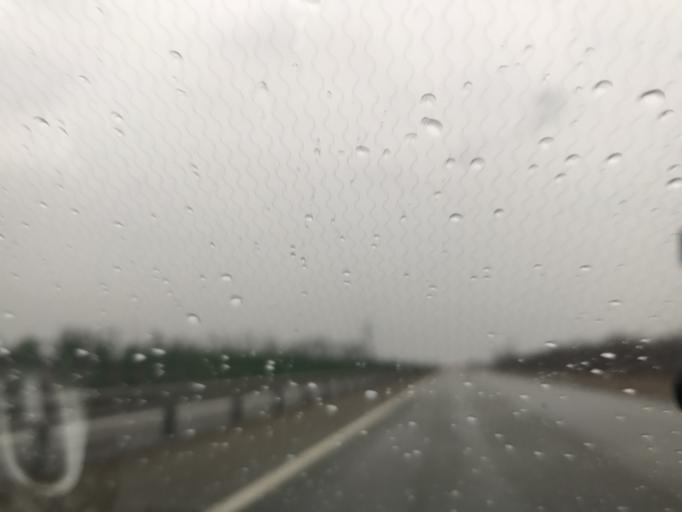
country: RU
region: Krasnodarskiy
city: Krylovskaya
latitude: 46.3092
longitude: 39.8075
